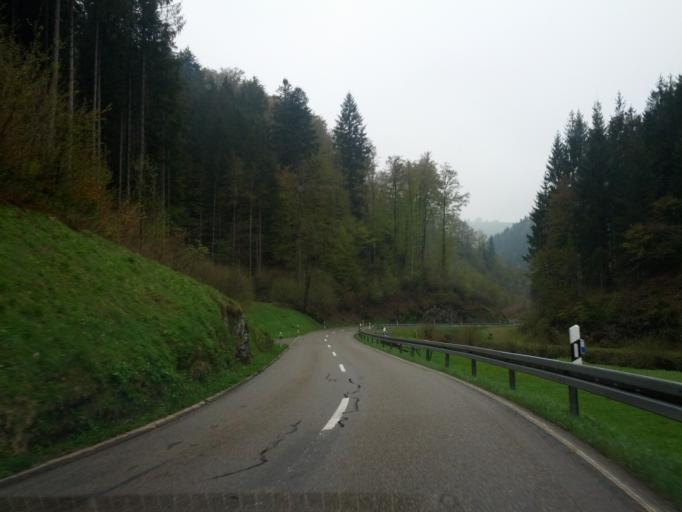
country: DE
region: Baden-Wuerttemberg
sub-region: Freiburg Region
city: Wieden
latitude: 47.8298
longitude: 7.8969
